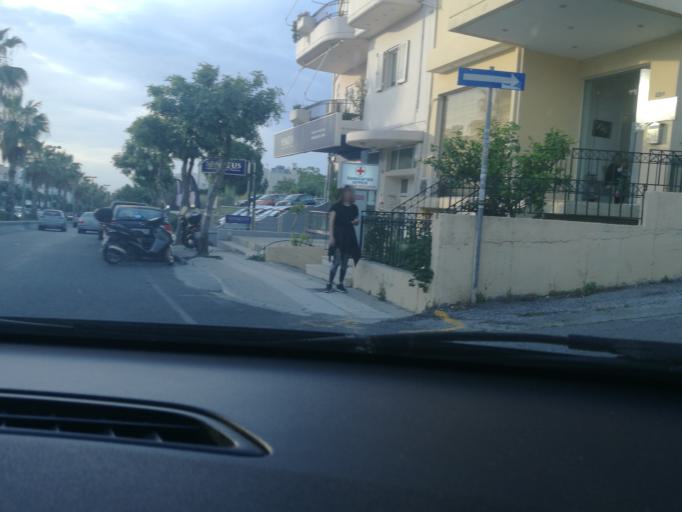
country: GR
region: Crete
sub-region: Nomos Irakleiou
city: Irakleion
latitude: 35.3169
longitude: 25.1460
